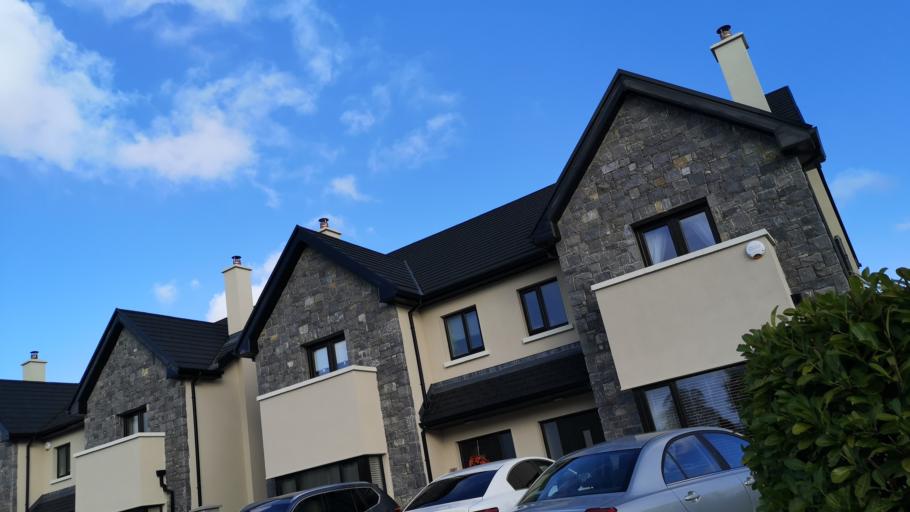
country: IE
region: Connaught
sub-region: County Galway
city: Athenry
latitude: 53.3012
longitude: -8.7612
